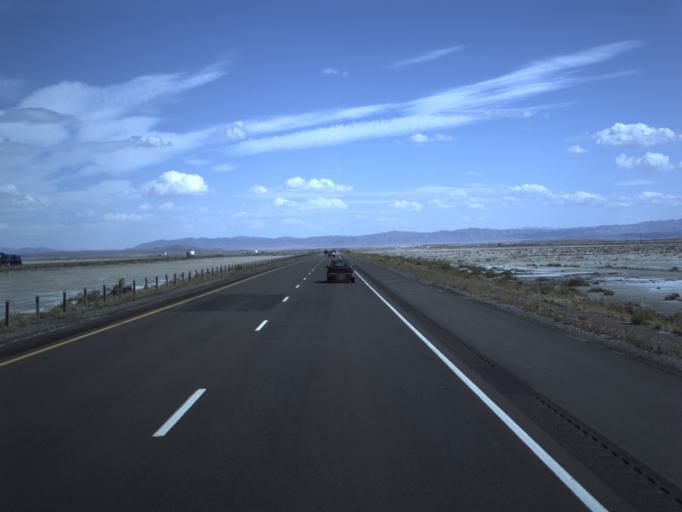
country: US
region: Utah
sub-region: Tooele County
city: Wendover
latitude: 40.7274
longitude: -113.3217
